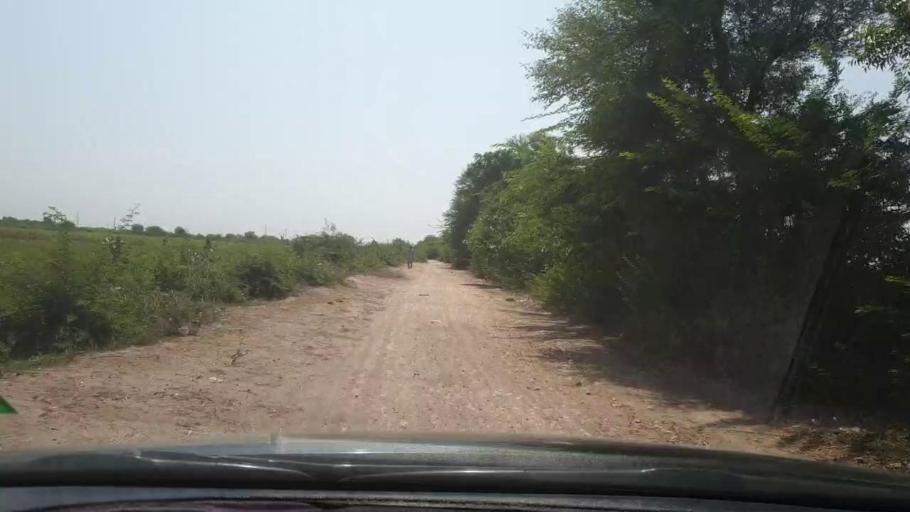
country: PK
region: Sindh
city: Tando Bago
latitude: 24.7811
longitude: 69.1825
